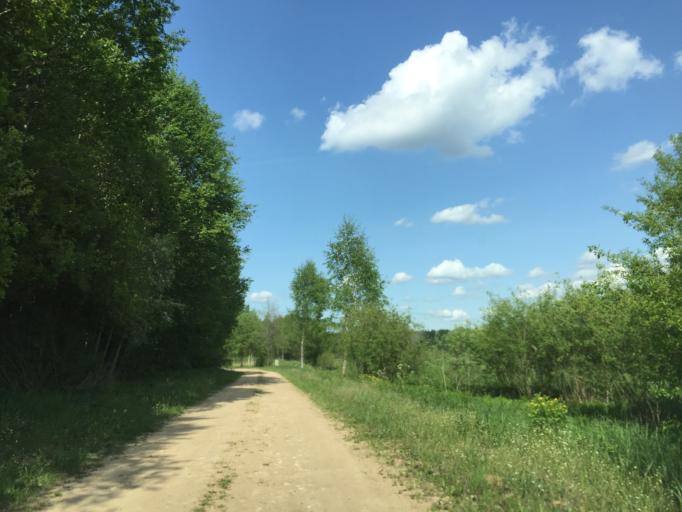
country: LV
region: Baldone
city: Baldone
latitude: 56.7923
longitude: 24.4202
